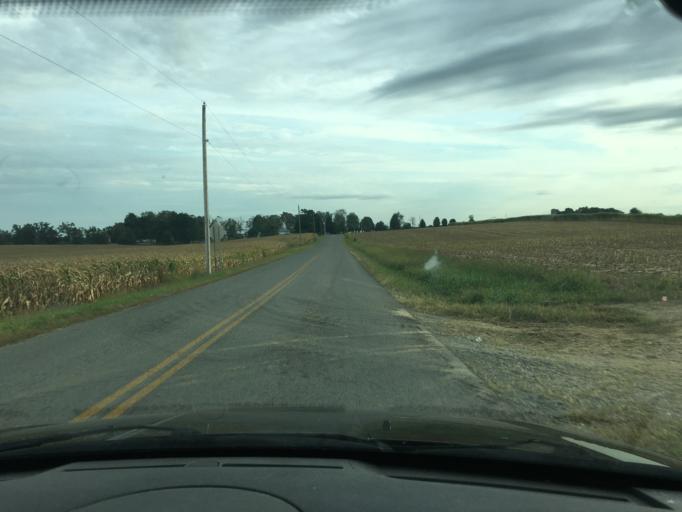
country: US
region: Ohio
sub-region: Logan County
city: West Liberty
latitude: 40.2948
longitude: -83.6847
